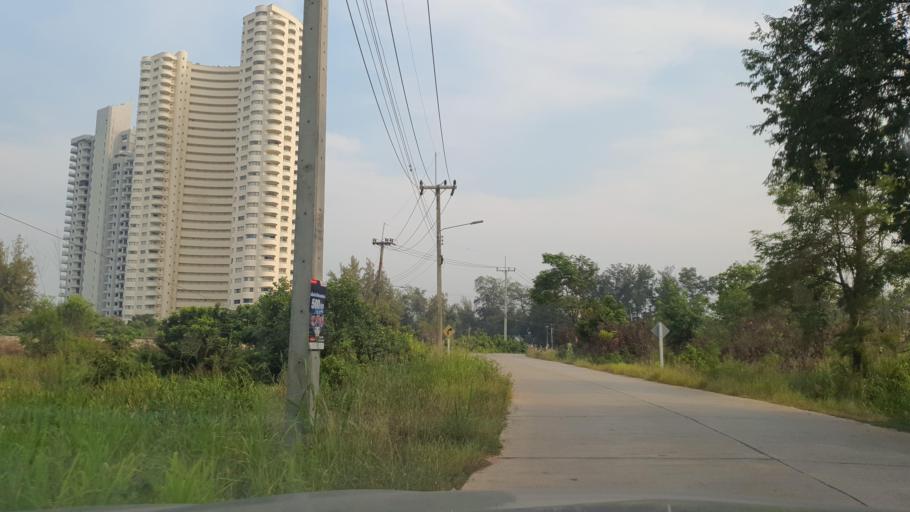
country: TH
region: Rayong
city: Rayong
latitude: 12.6056
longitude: 101.3994
